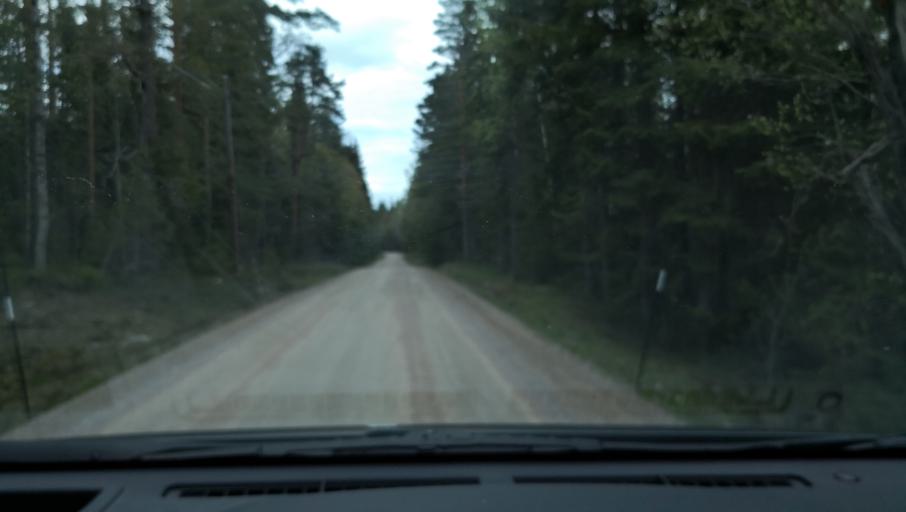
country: SE
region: Vaestmanland
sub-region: Fagersta Kommun
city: Fagersta
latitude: 60.0954
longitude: 15.7906
